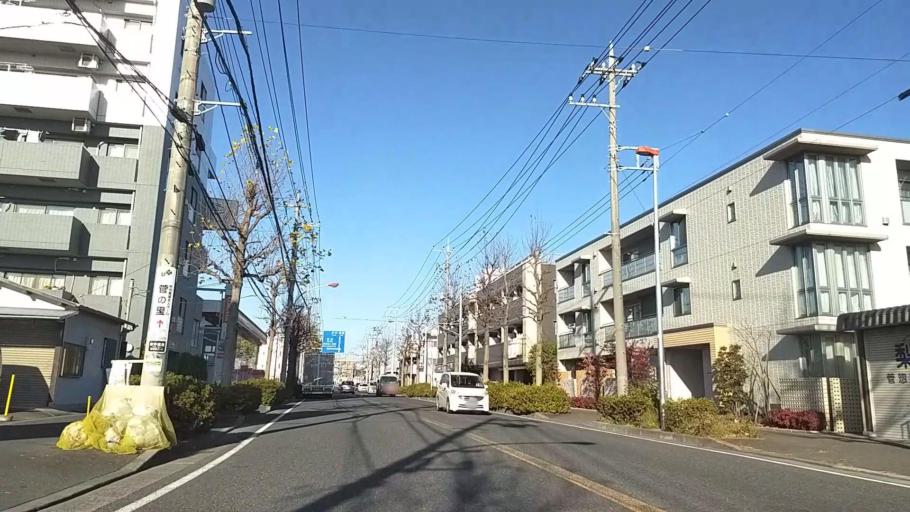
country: JP
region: Tokyo
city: Chofugaoka
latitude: 35.6276
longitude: 139.5412
